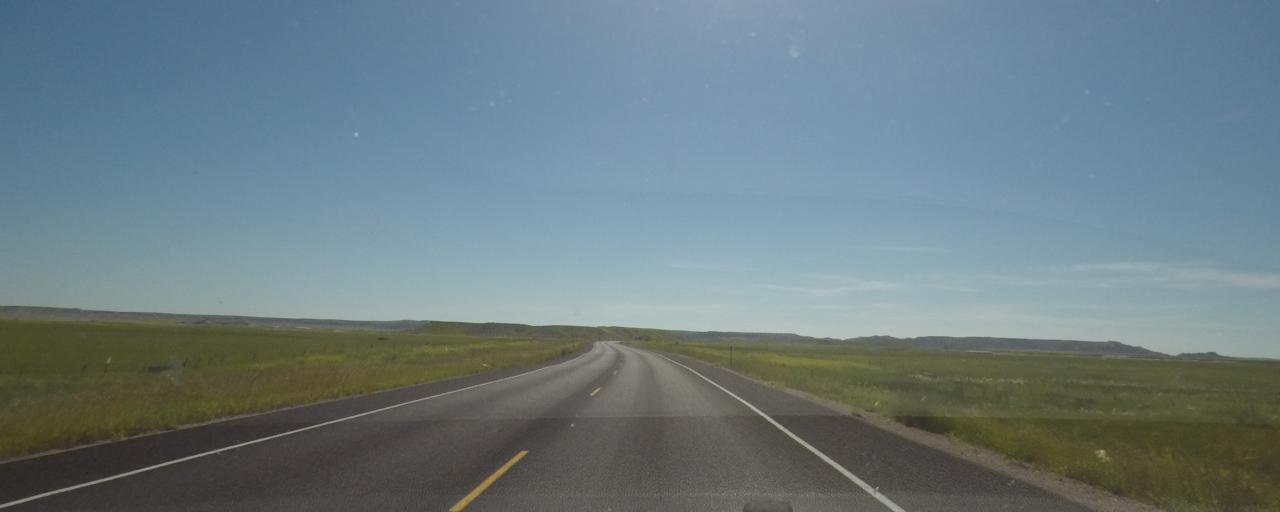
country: US
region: South Dakota
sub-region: Shannon County
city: Porcupine
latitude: 43.7784
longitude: -102.5423
